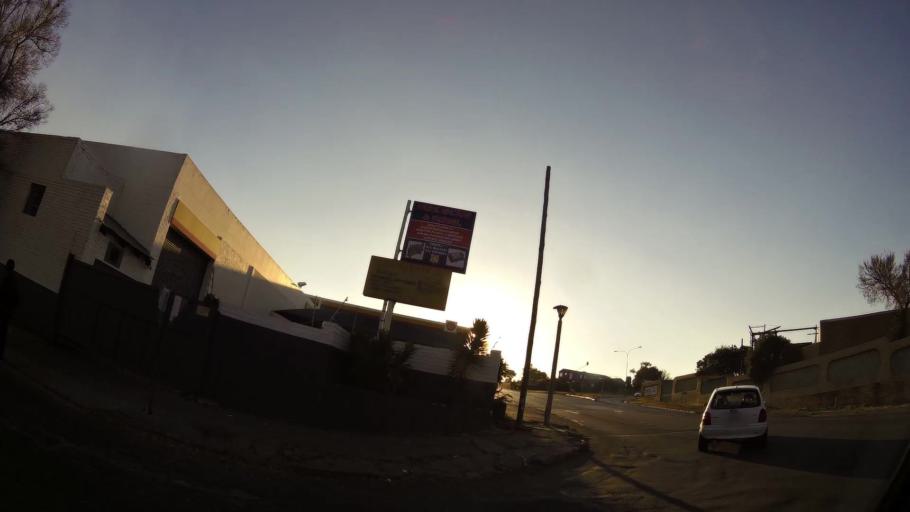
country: ZA
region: Gauteng
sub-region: Ekurhuleni Metropolitan Municipality
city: Germiston
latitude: -26.2528
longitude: 28.1323
